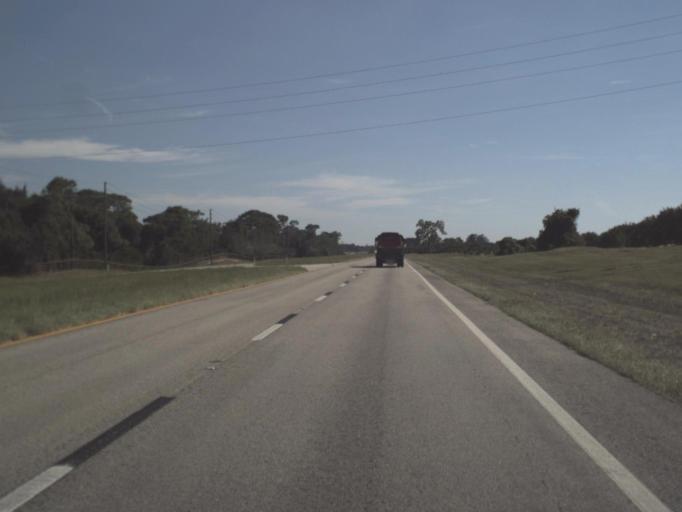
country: US
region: Florida
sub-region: Highlands County
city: Lake Placid
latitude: 27.2483
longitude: -81.3383
